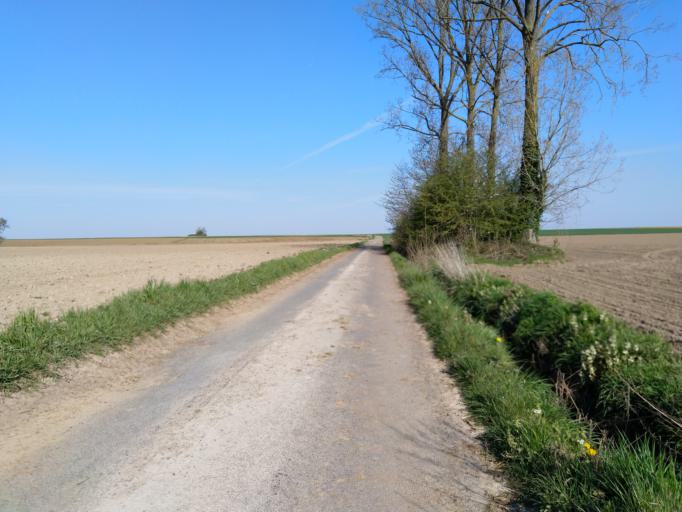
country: BE
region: Wallonia
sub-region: Province du Hainaut
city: Lens
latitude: 50.5564
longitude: 3.8807
